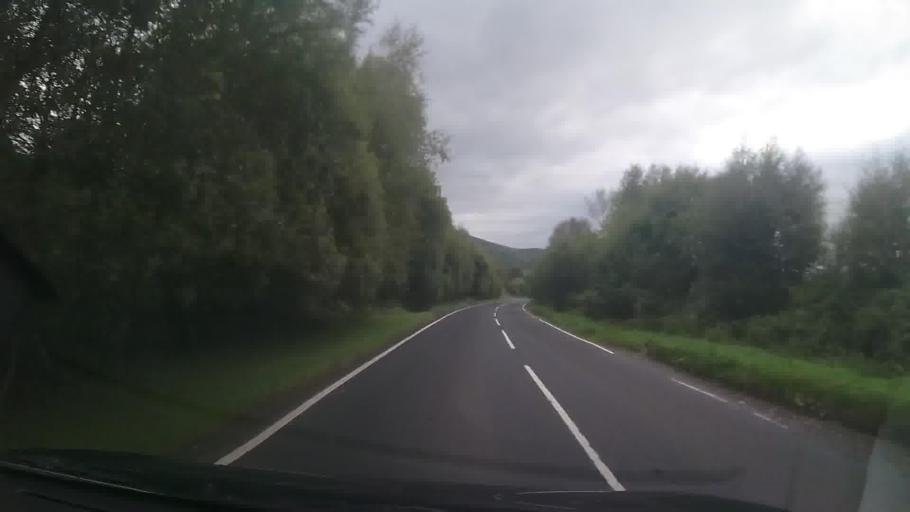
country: GB
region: Scotland
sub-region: Argyll and Bute
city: Garelochhead
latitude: 56.2304
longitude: -4.9757
